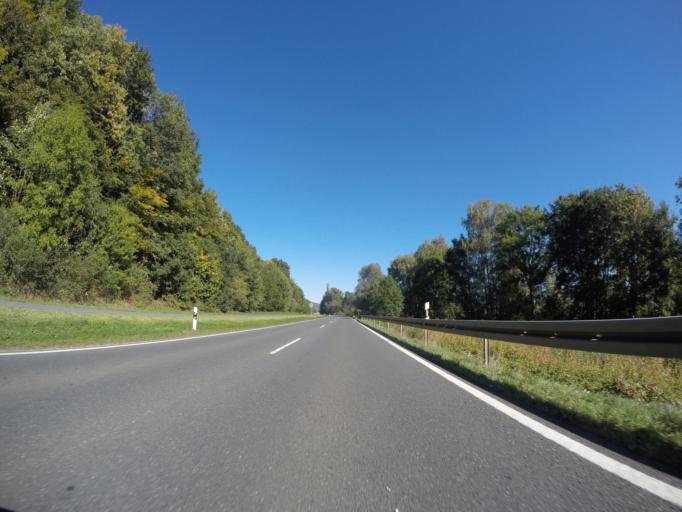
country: DE
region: Bavaria
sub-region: Upper Franconia
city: Wiesenthau
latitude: 49.7277
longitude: 11.1248
